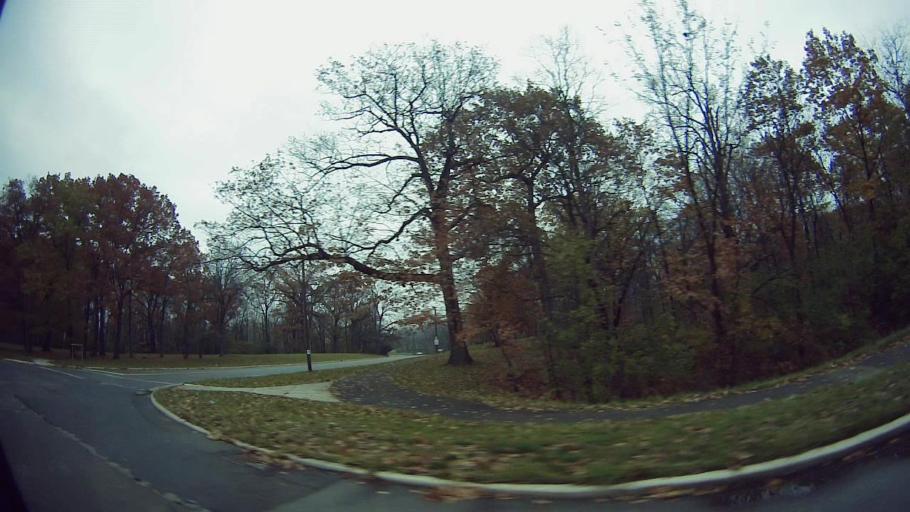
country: US
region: Michigan
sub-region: Wayne County
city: Dearborn Heights
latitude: 42.3512
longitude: -83.2546
